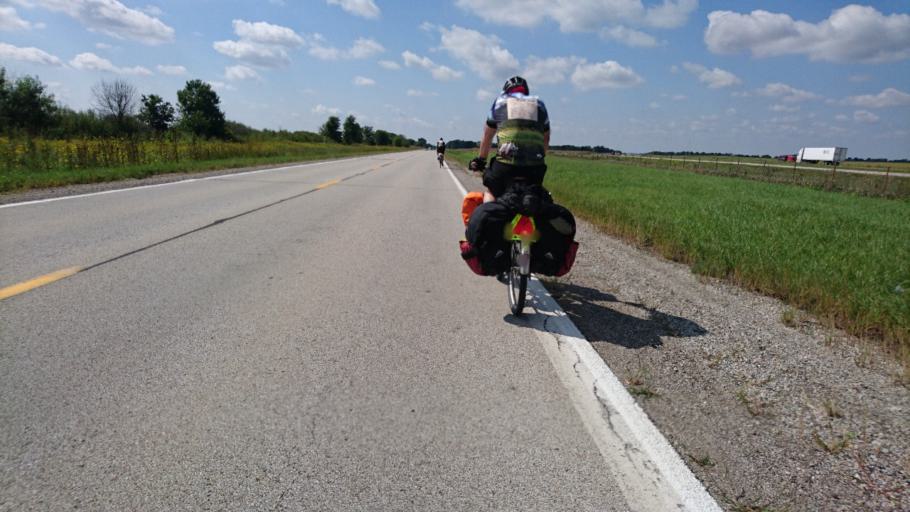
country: US
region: Illinois
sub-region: McLean County
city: Lexington
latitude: 40.5902
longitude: -88.8597
